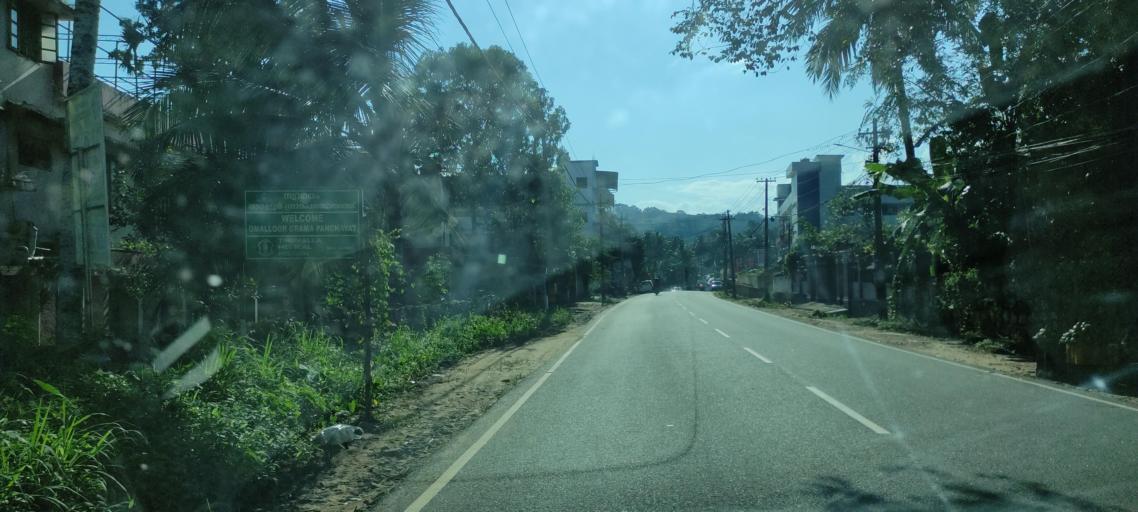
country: IN
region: Kerala
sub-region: Pattanamtitta
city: Pathanamthitta
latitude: 9.2566
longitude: 76.7729
